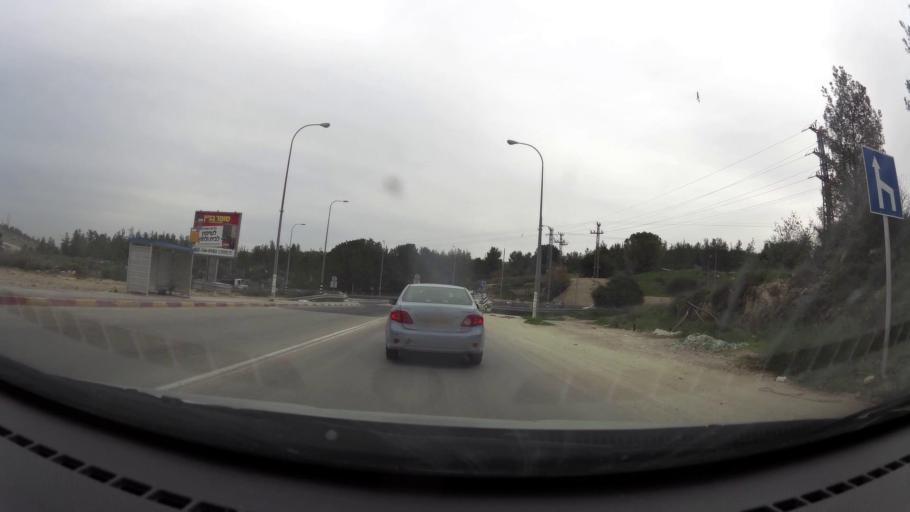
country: IL
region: Jerusalem
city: Bet Shemesh
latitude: 31.7045
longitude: 35.0083
